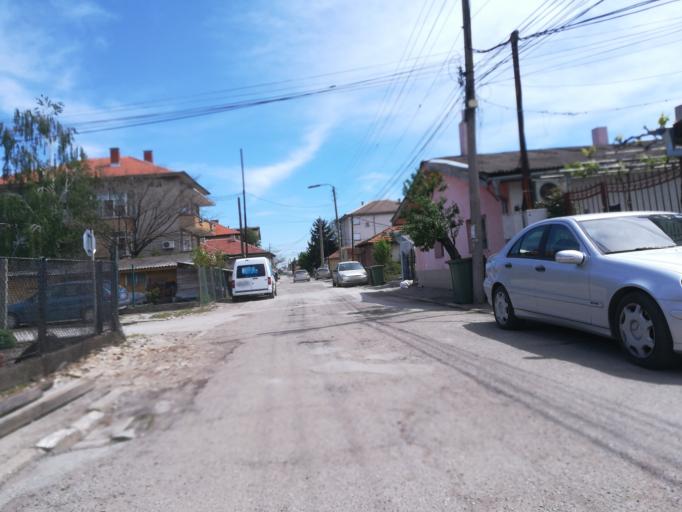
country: BG
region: Stara Zagora
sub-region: Obshtina Chirpan
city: Chirpan
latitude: 42.0942
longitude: 25.2261
